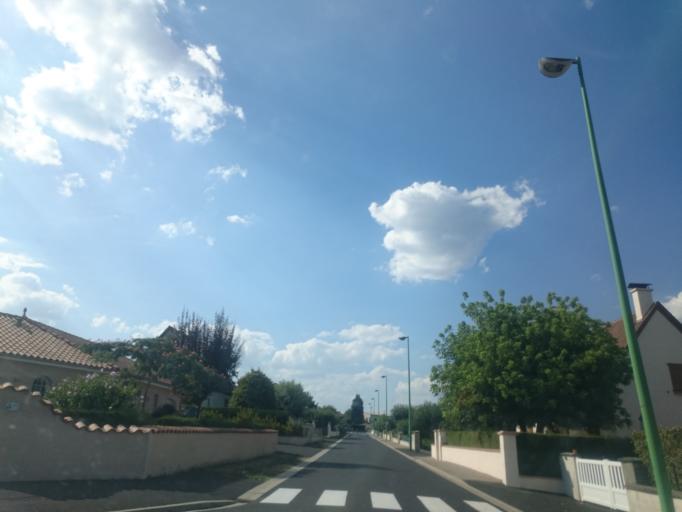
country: FR
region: Auvergne
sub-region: Departement du Cantal
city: Saint-Mamet-la-Salvetat
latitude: 44.8569
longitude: 2.2284
